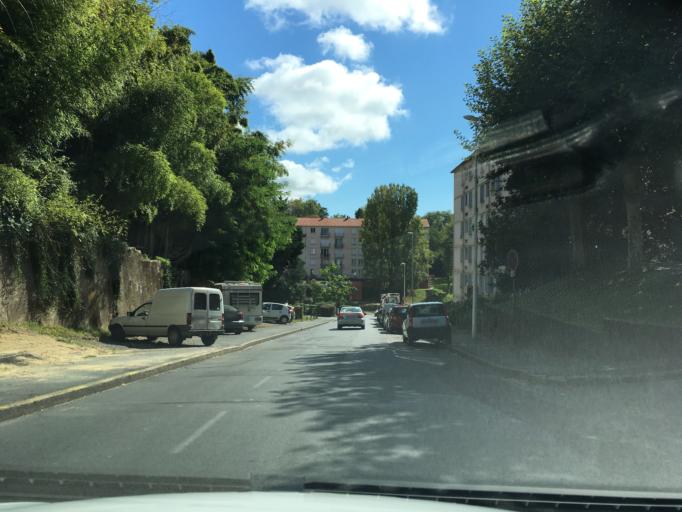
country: FR
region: Aquitaine
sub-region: Departement des Pyrenees-Atlantiques
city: Bayonne
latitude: 43.5000
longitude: -1.4662
